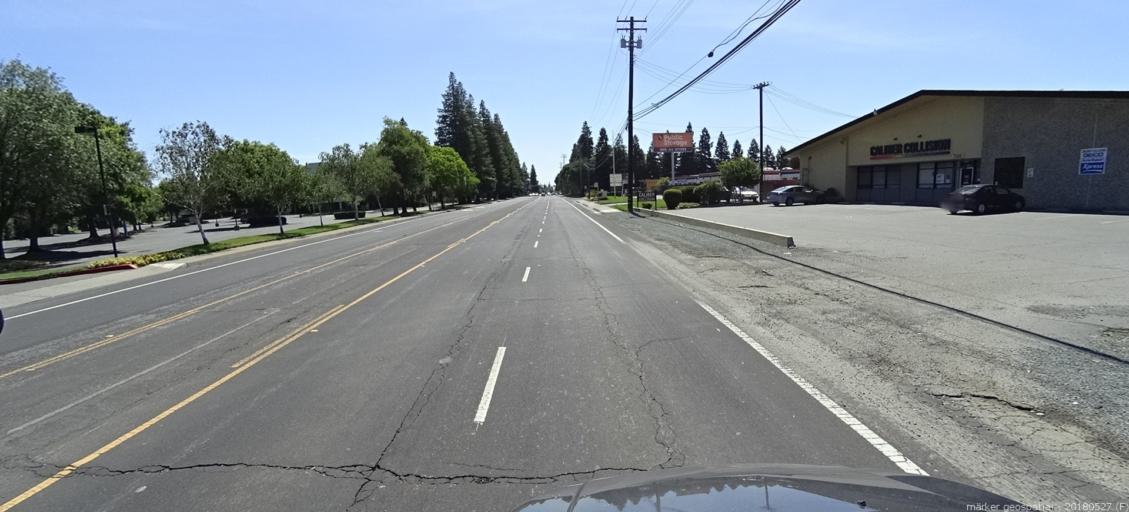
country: US
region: California
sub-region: Sacramento County
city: Rosemont
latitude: 38.5512
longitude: -121.4170
